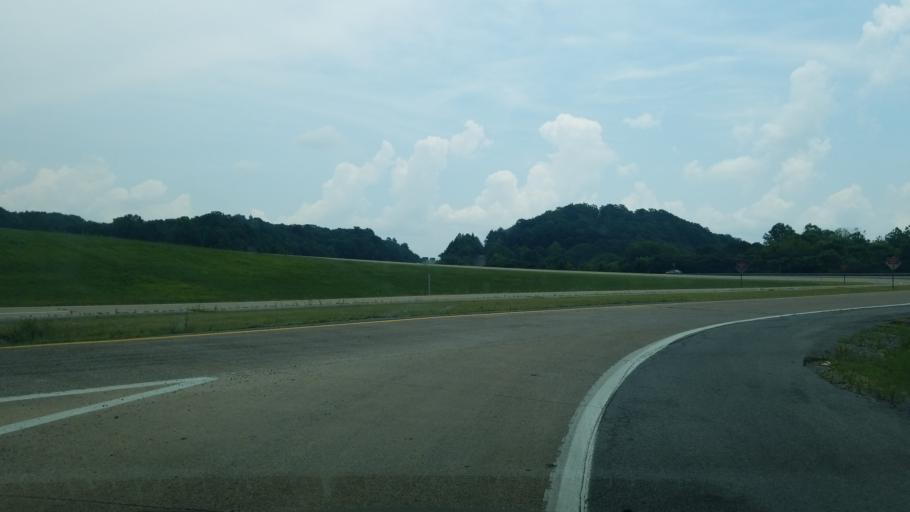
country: US
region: Tennessee
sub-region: Hamilton County
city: Soddy-Daisy
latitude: 35.3037
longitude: -85.1637
